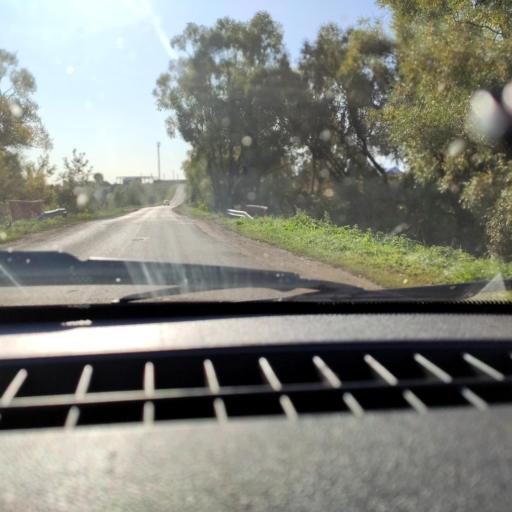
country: RU
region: Bashkortostan
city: Avdon
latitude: 54.6044
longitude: 55.7950
